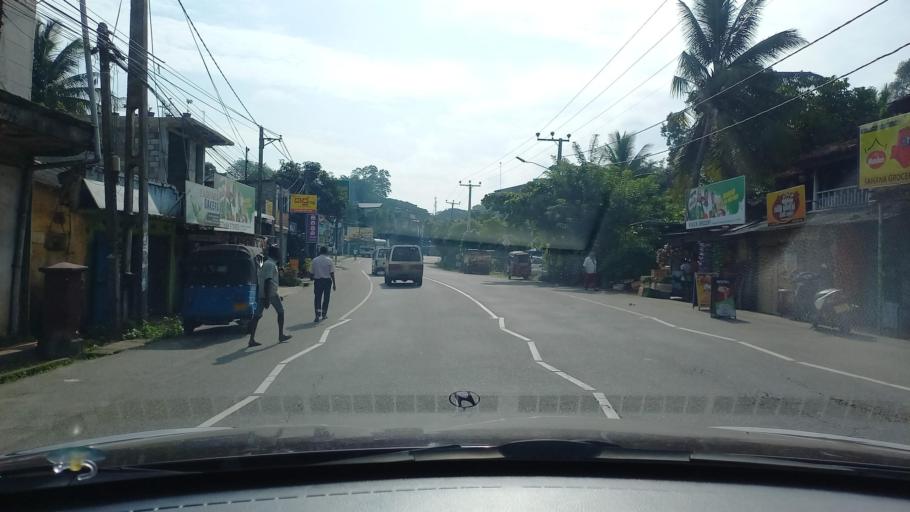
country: LK
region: Central
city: Kadugannawa
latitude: 7.2657
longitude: 80.5636
